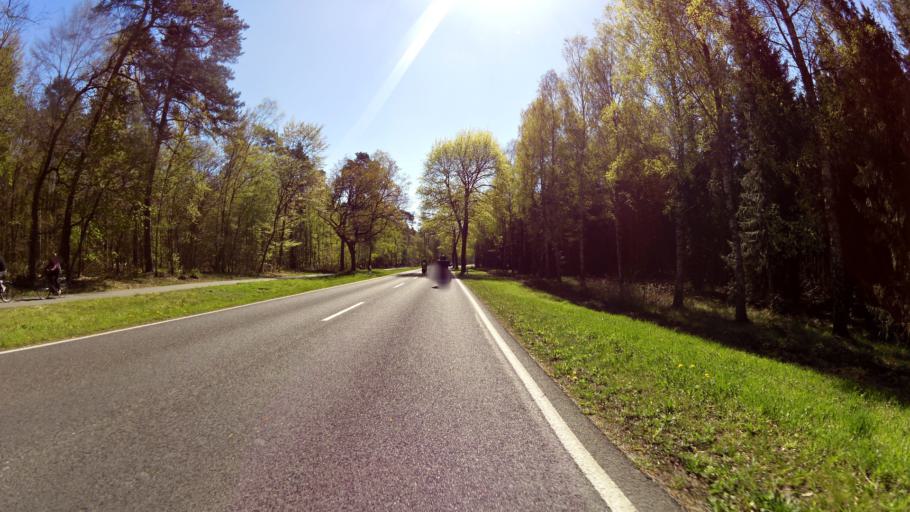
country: DE
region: Brandenburg
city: Bernau bei Berlin
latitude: 52.7148
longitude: 13.5290
